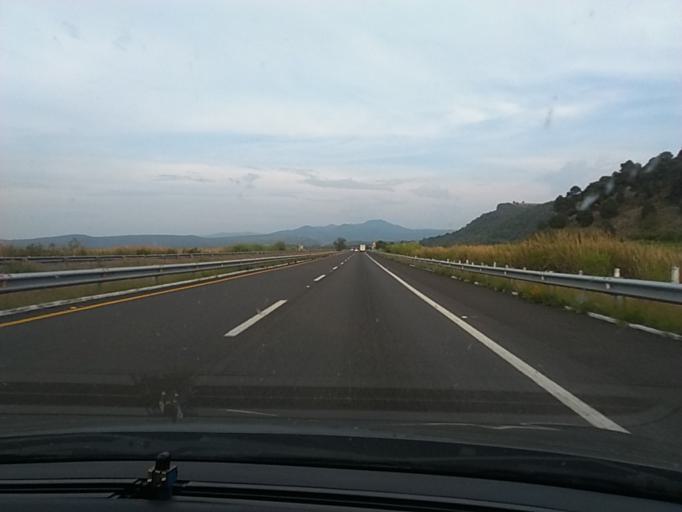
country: MX
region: Michoacan
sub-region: Zinapecuaro
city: Jose Maria Morelos (La Yegueeria)
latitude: 19.9001
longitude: -100.8692
